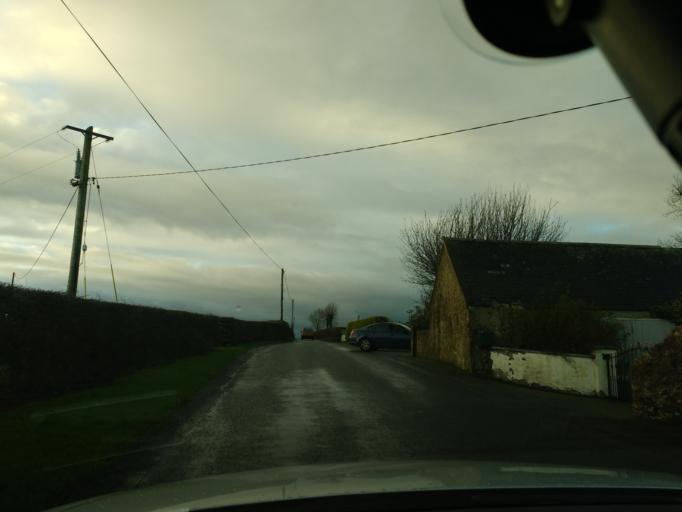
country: IE
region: Munster
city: Thurles
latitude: 52.6318
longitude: -7.7904
